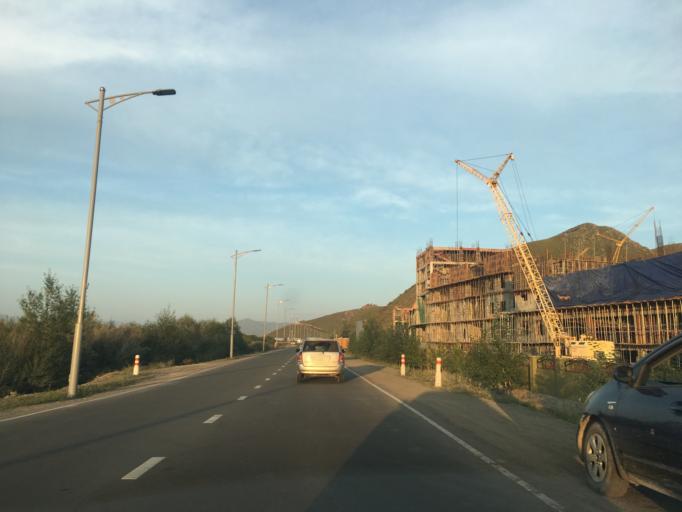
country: MN
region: Ulaanbaatar
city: Ulaanbaatar
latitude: 47.8827
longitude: 106.9601
